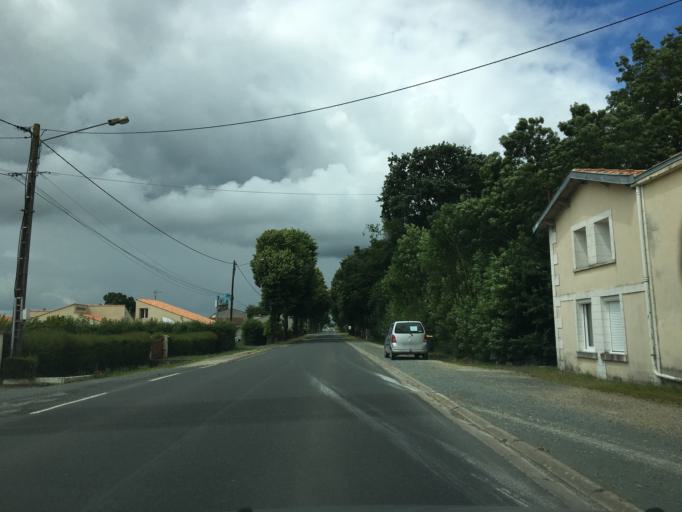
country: FR
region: Poitou-Charentes
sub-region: Departement des Deux-Sevres
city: Beauvoir-sur-Niort
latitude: 46.0920
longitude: -0.5039
